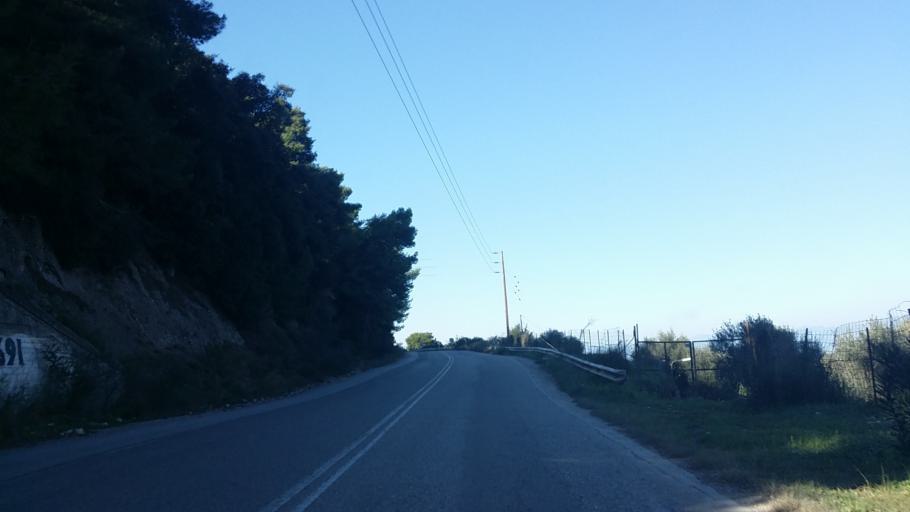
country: GR
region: West Greece
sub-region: Nomos Achaias
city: Akrata
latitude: 38.1802
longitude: 22.2147
